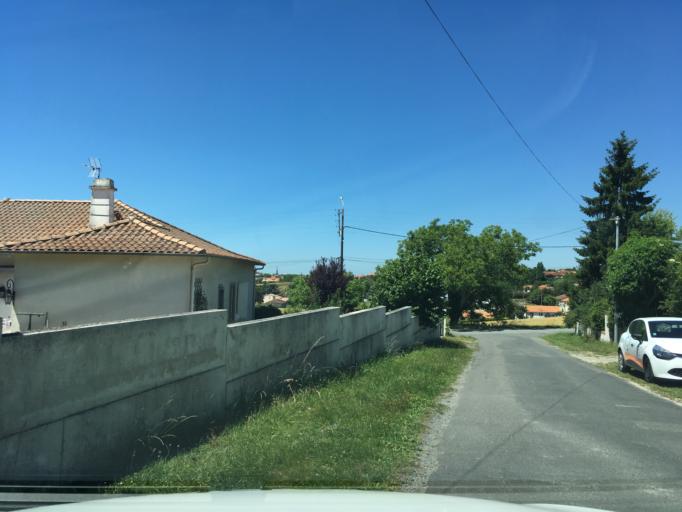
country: FR
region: Poitou-Charentes
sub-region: Departement des Deux-Sevres
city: Aiffres
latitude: 46.3195
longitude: -0.4227
